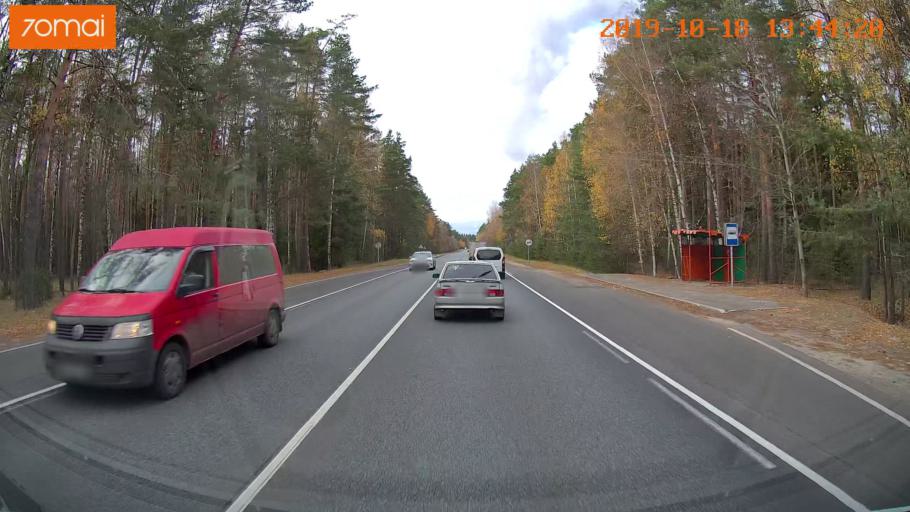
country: RU
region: Rjazan
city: Solotcha
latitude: 54.9362
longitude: 39.9639
